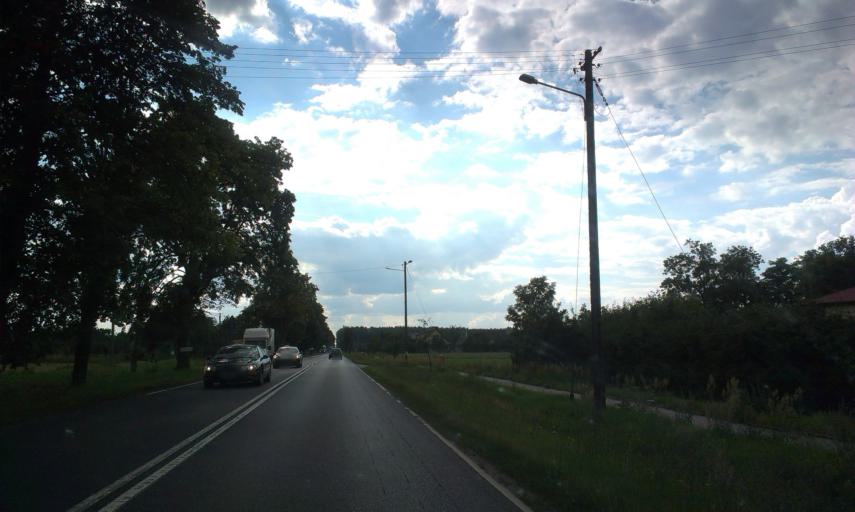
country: PL
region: Greater Poland Voivodeship
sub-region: Powiat pilski
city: Miasteczko Krajenskie
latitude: 53.1322
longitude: 17.0056
